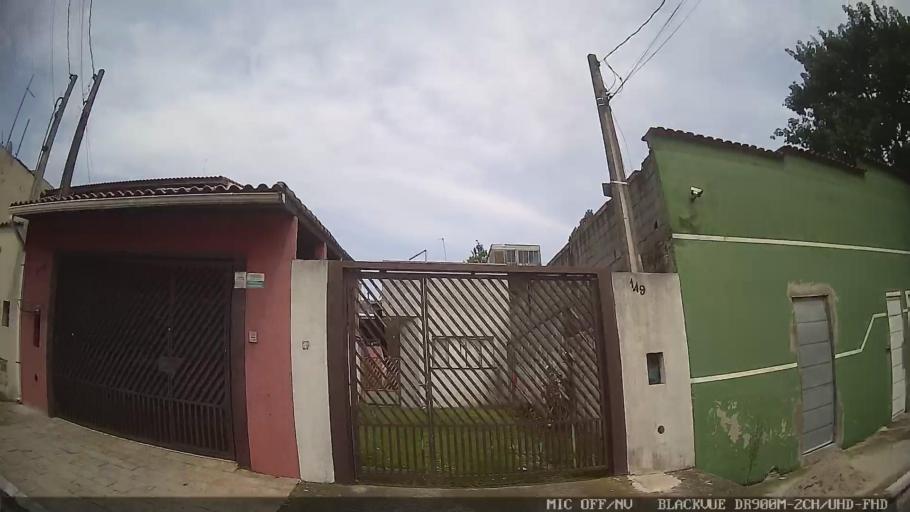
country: BR
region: Sao Paulo
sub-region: Poa
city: Poa
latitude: -23.5170
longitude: -46.3594
